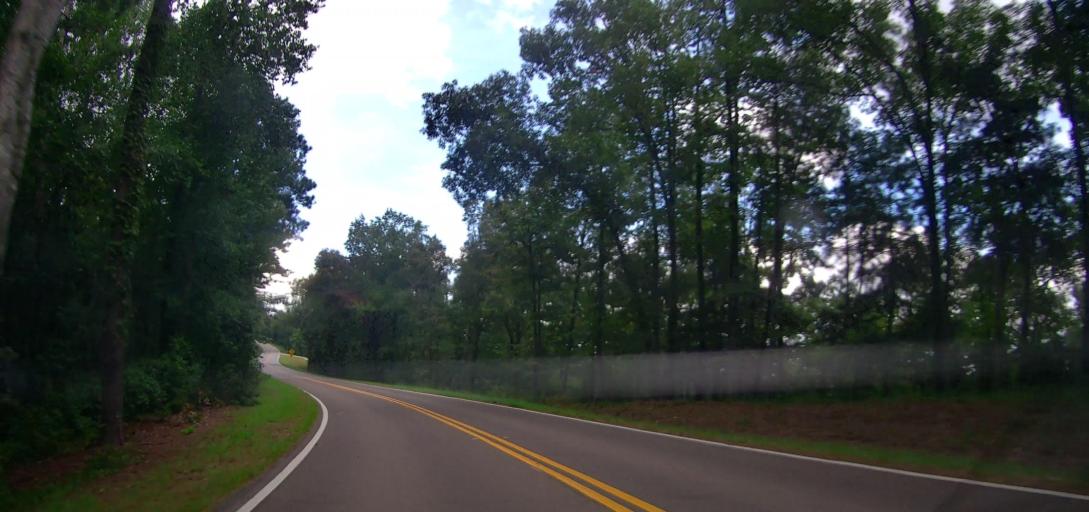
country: US
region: Georgia
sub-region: Harris County
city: Pine Mountain
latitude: 32.8409
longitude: -84.8044
